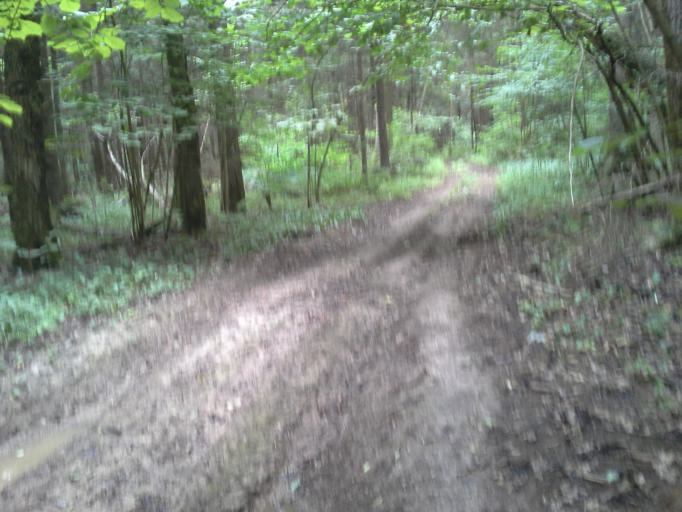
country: RU
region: Moskovskaya
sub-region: Leninskiy Rayon
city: Vnukovo
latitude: 55.6438
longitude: 37.2961
